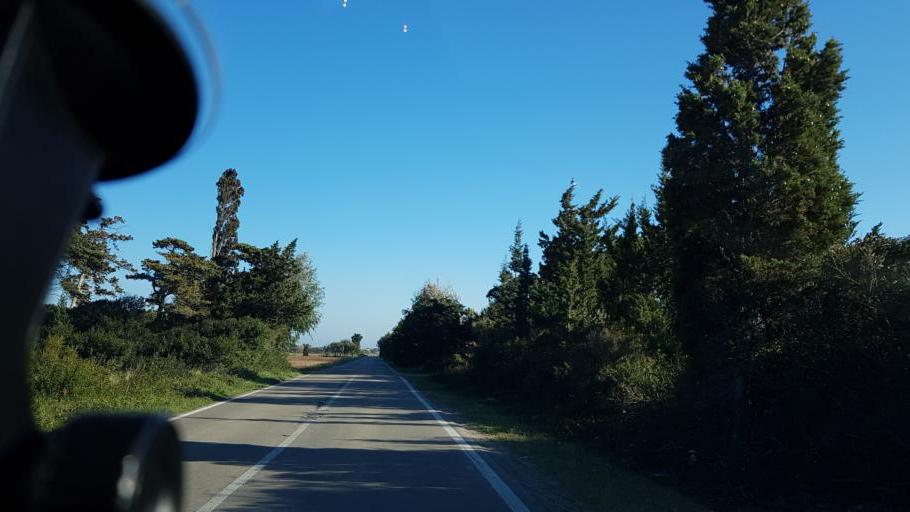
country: IT
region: Apulia
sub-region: Provincia di Lecce
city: Giorgilorio
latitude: 40.4430
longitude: 18.2320
